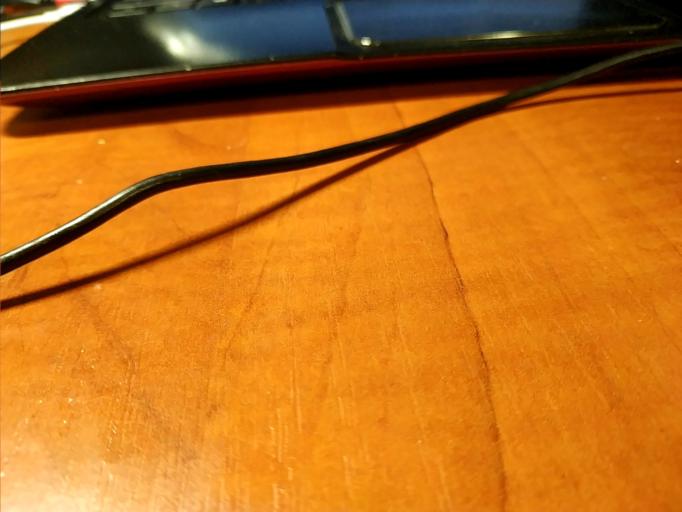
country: RU
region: Tverskaya
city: Rameshki
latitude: 57.2194
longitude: 36.0922
